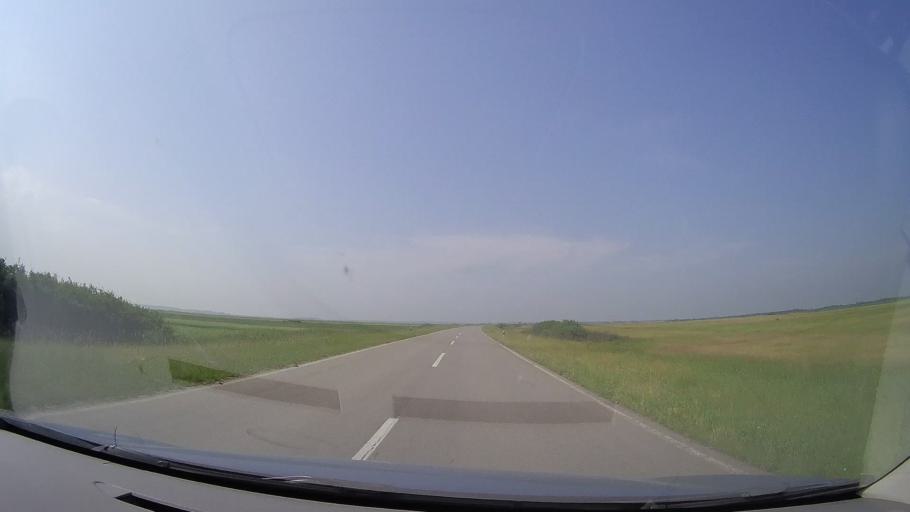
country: RS
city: Jasa Tomic
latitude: 45.4175
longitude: 20.8333
